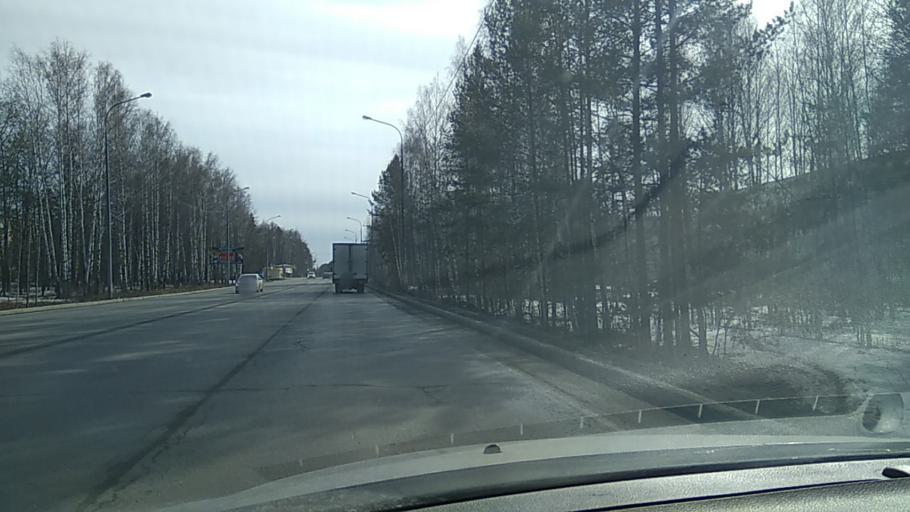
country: RU
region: Sverdlovsk
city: Nikolo-Pavlovskoye
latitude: 57.8557
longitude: 60.0312
